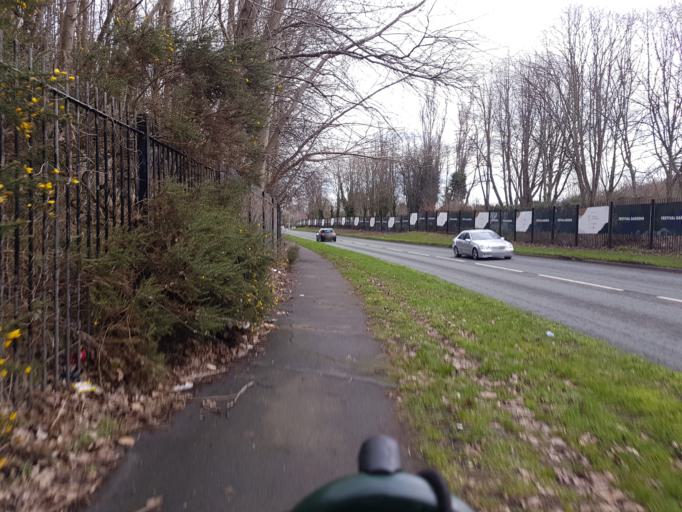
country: GB
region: England
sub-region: Metropolitan Borough of Wirral
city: Bromborough
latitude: 53.3742
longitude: -2.9623
